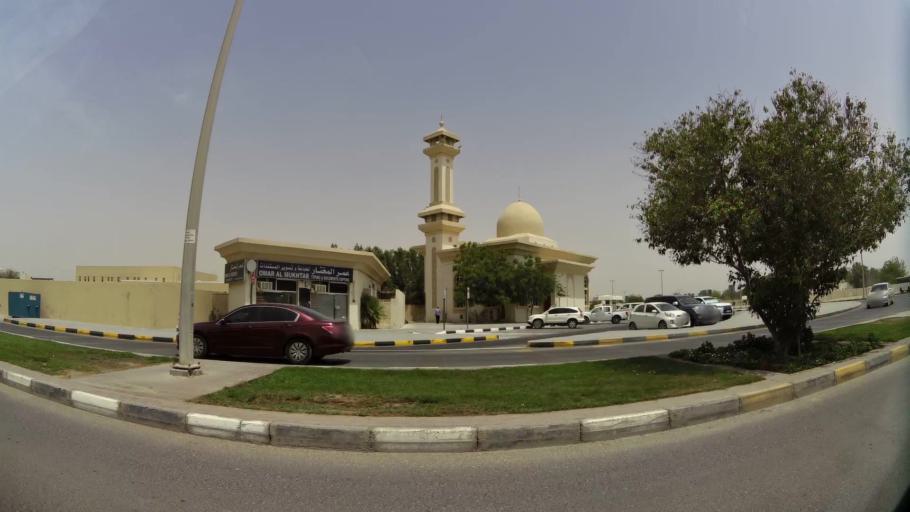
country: AE
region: Ash Shariqah
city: Sharjah
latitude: 25.3504
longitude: 55.4055
